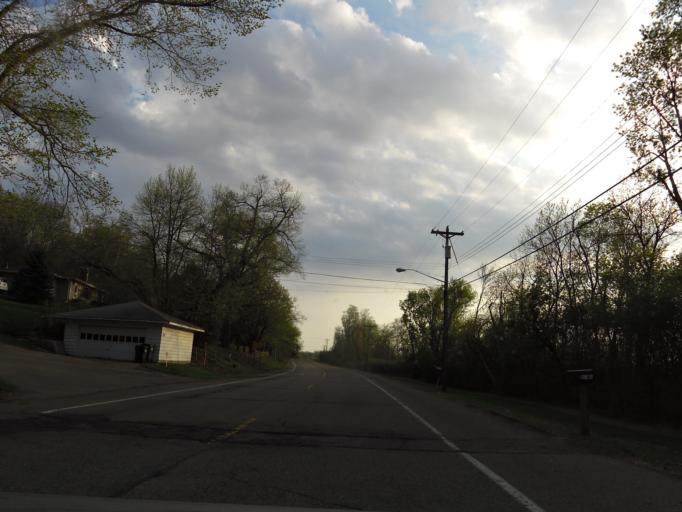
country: US
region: Minnesota
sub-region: Dakota County
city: Mendota Heights
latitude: 44.8943
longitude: -93.1498
